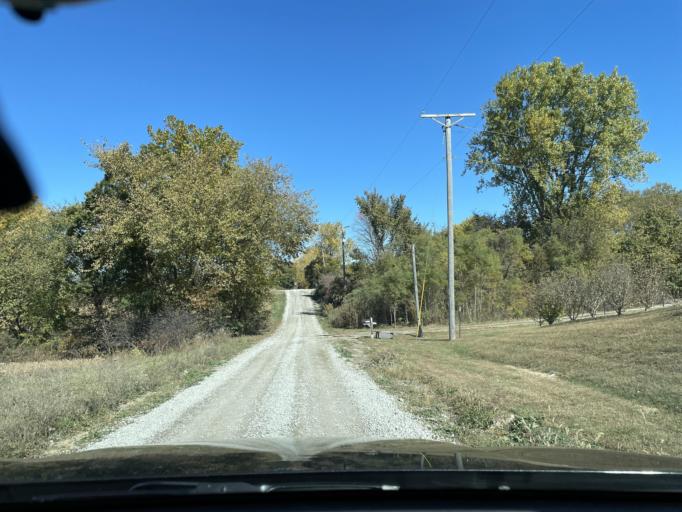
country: US
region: Missouri
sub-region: Andrew County
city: Savannah
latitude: 39.9345
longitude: -94.8804
